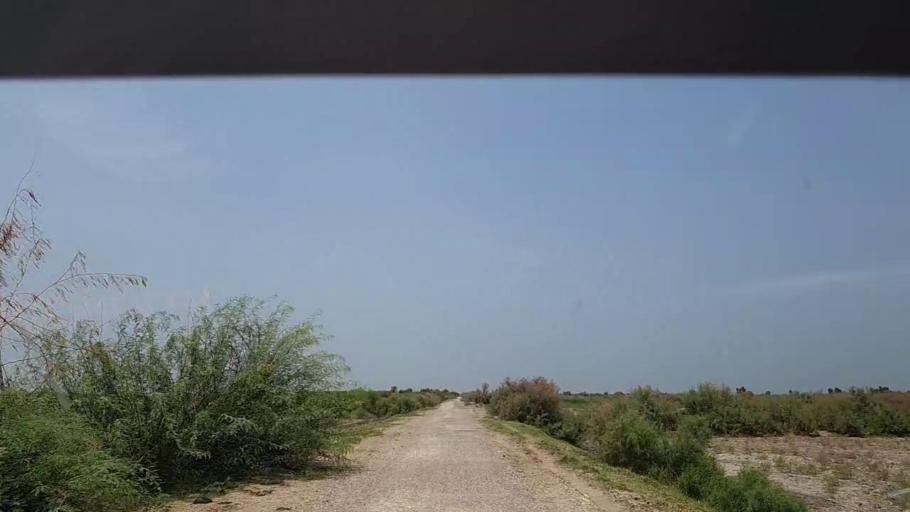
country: PK
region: Sindh
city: Adilpur
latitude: 27.8888
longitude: 69.2541
